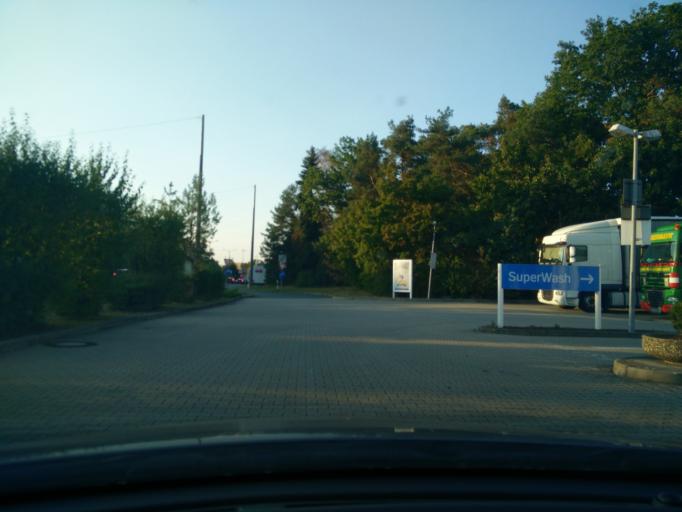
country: DE
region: Bavaria
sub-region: Regierungsbezirk Mittelfranken
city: Wendelstein
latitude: 49.4017
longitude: 11.1157
